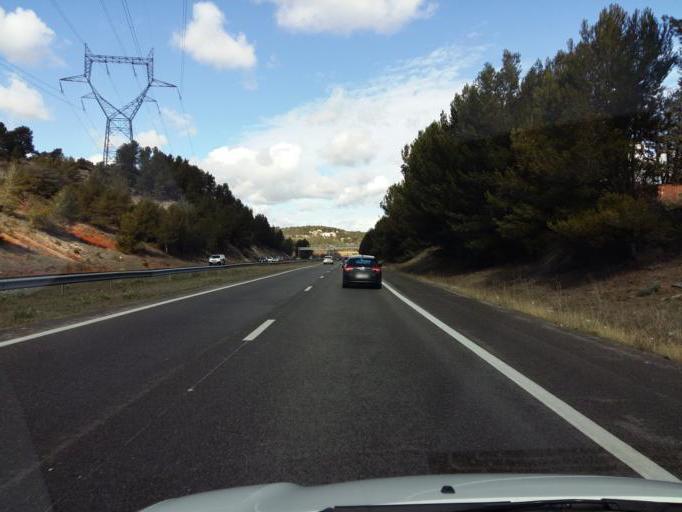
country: FR
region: Provence-Alpes-Cote d'Azur
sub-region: Departement des Bouches-du-Rhone
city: Cabries
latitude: 43.4438
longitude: 5.3962
